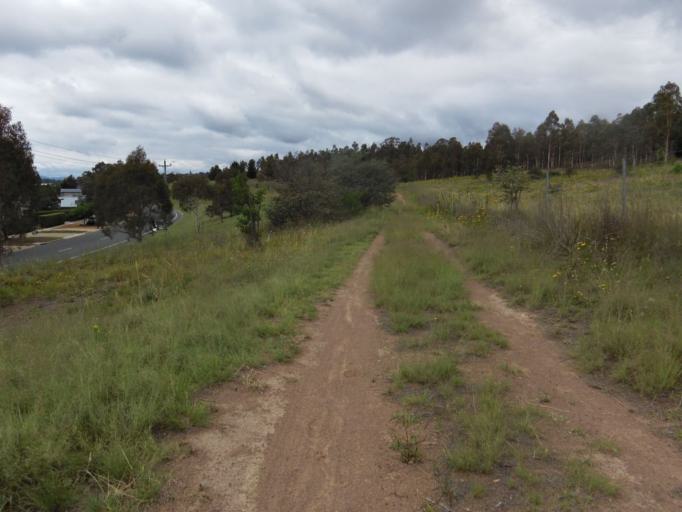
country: AU
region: Australian Capital Territory
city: Macquarie
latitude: -35.3367
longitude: 149.0261
